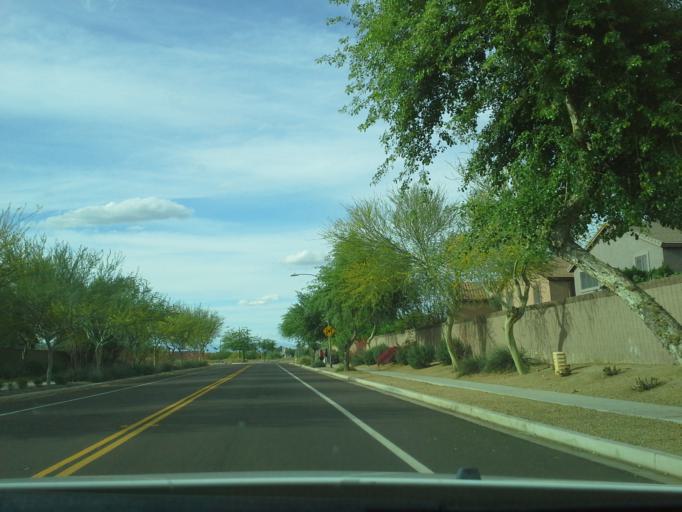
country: US
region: Arizona
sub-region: Maricopa County
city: Peoria
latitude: 33.6332
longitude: -112.2155
